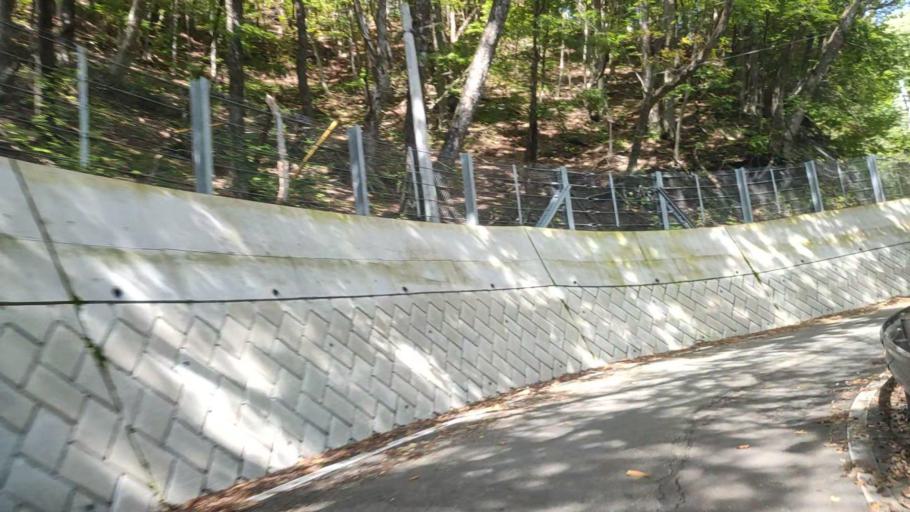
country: JP
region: Gunma
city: Nakanojomachi
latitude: 36.6426
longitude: 138.6115
